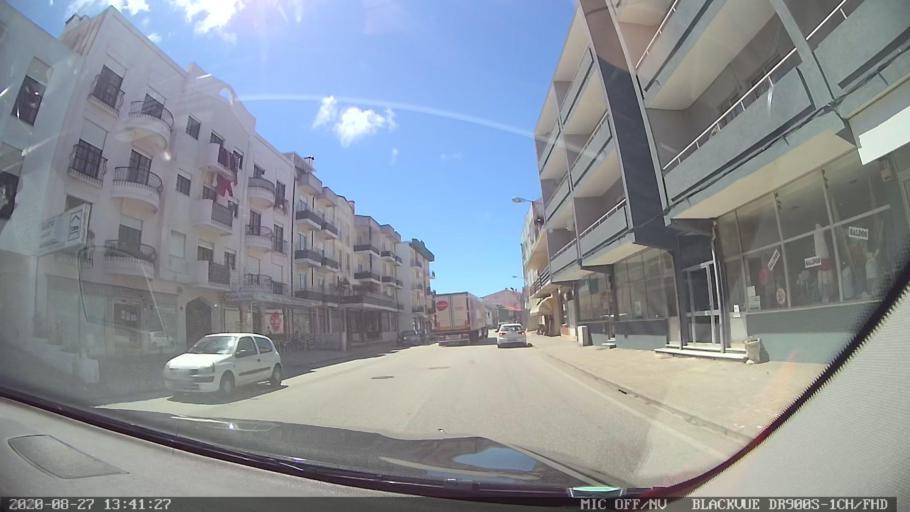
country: PT
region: Coimbra
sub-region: Mira
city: Mira
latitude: 40.4297
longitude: -8.7331
